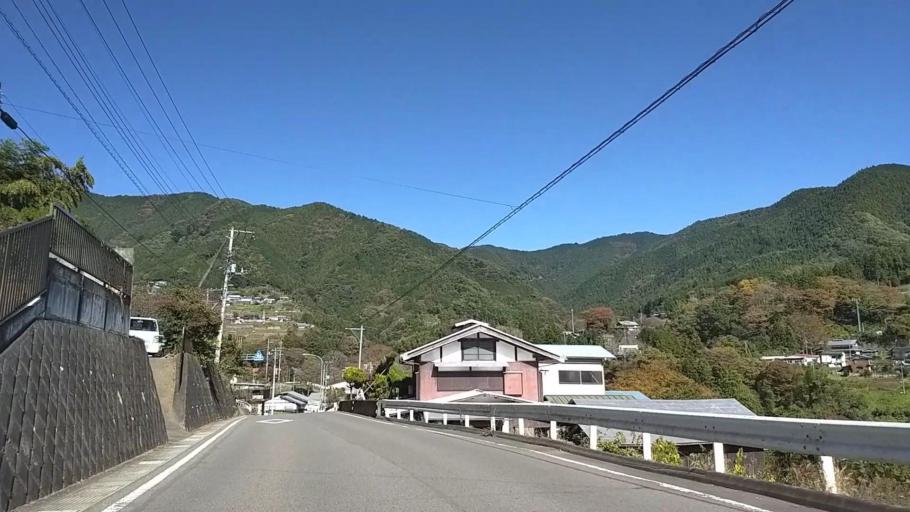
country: JP
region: Yamanashi
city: Uenohara
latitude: 35.6688
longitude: 139.0887
